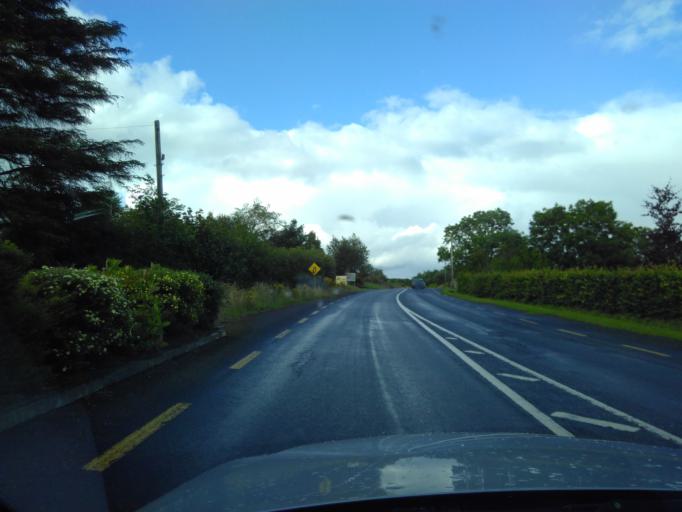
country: IE
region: Ulster
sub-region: County Donegal
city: Ramelton
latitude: 54.9866
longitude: -7.6694
